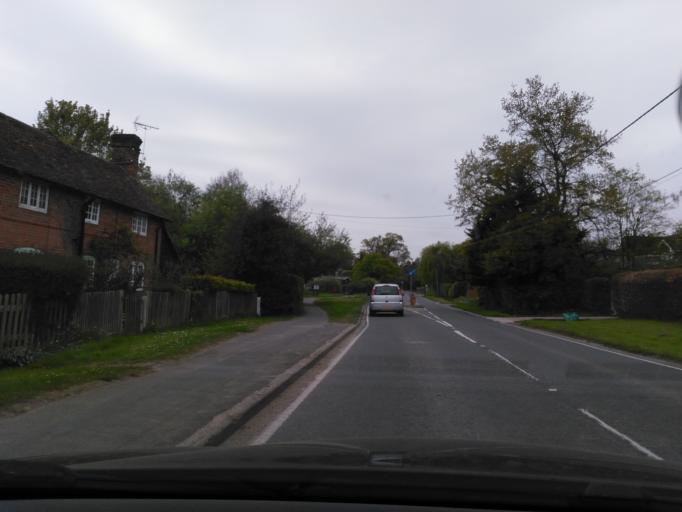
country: GB
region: England
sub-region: West Berkshire
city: Stratfield Mortimer
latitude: 51.3297
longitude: -1.0672
